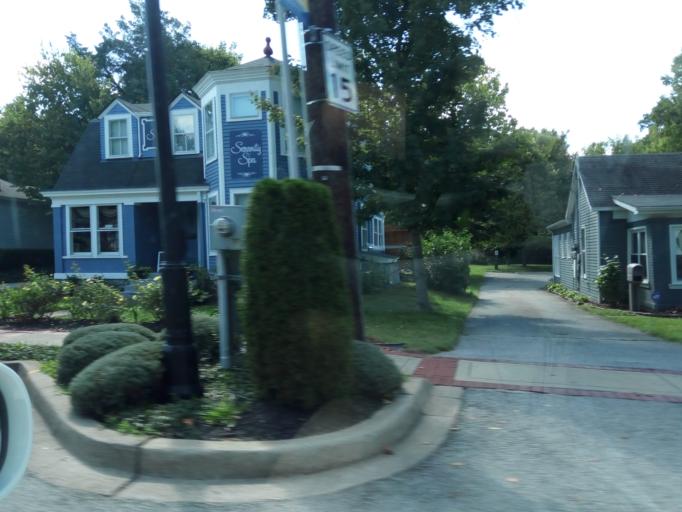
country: US
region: Kentucky
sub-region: Jefferson County
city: Middletown
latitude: 38.2451
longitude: -85.5407
